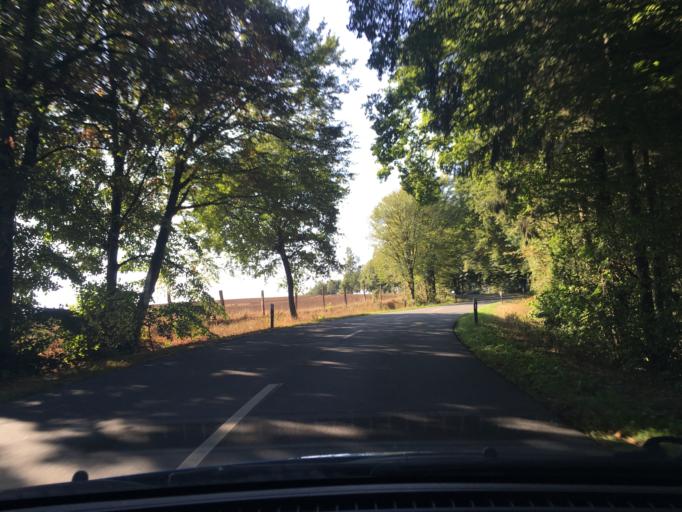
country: DE
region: Lower Saxony
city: Rehlingen
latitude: 53.0747
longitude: 10.2325
